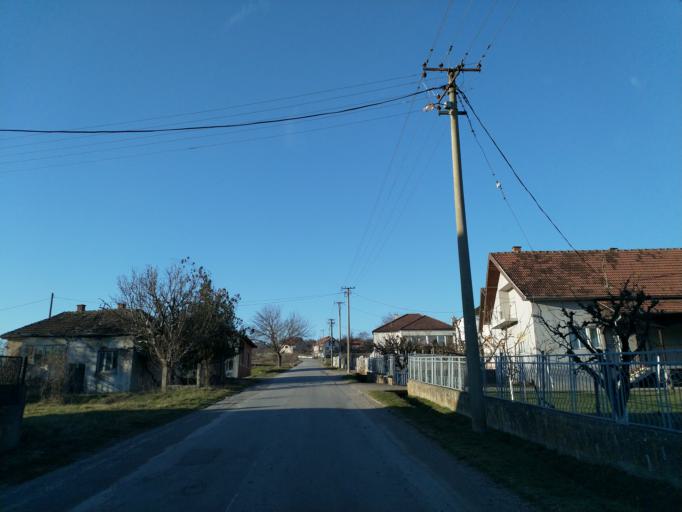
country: RS
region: Central Serbia
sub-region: Pomoravski Okrug
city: Paracin
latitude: 43.9207
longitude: 21.5107
